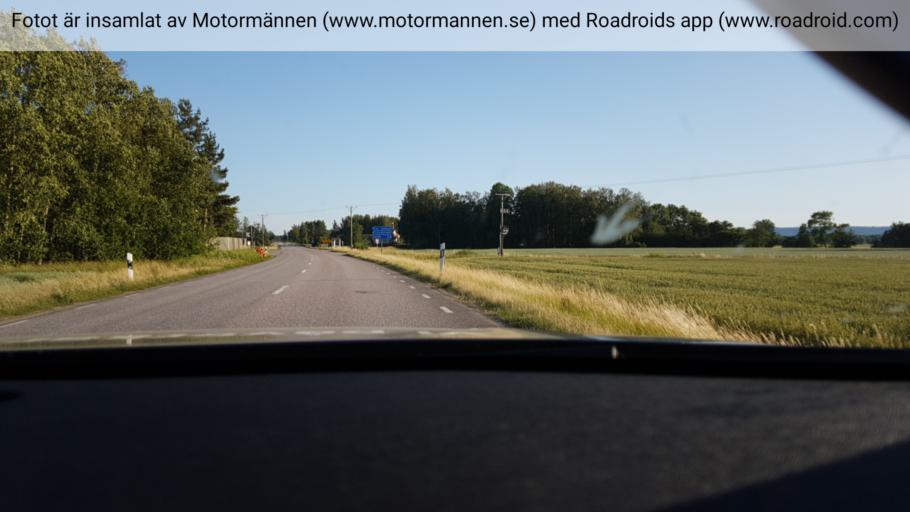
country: SE
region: Vaestra Goetaland
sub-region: Skovde Kommun
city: Stopen
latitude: 58.4892
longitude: 13.9610
